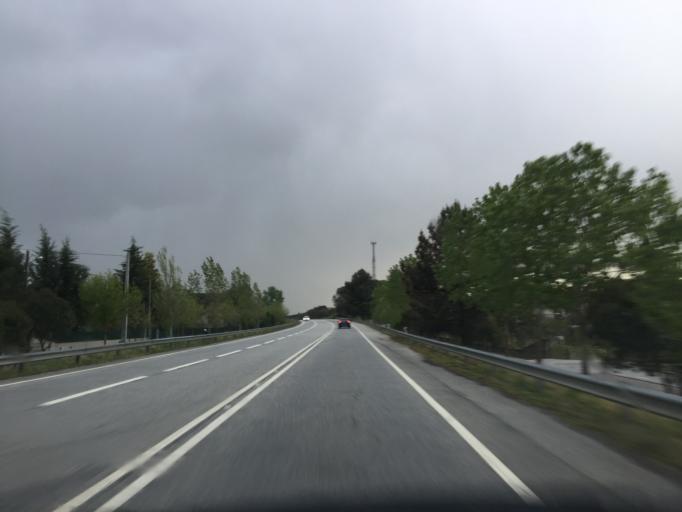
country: PT
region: Viseu
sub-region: Viseu
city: Viseu
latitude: 40.6125
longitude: -7.9585
